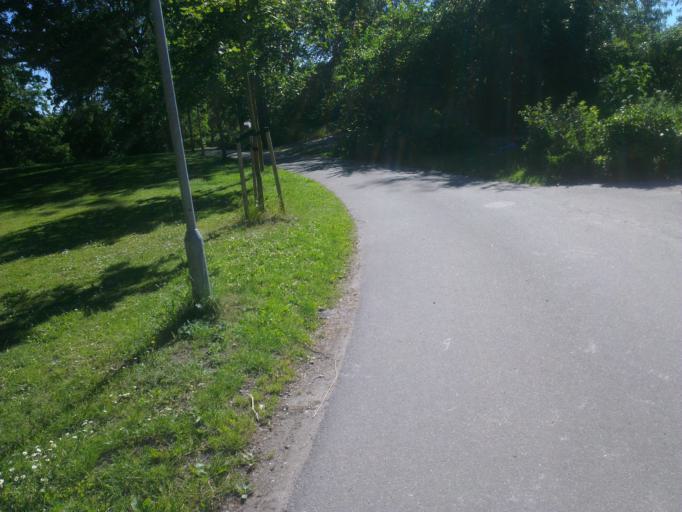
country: DK
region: Capital Region
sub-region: Frederikssund Kommune
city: Jaegerspris
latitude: 55.9068
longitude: 11.9201
